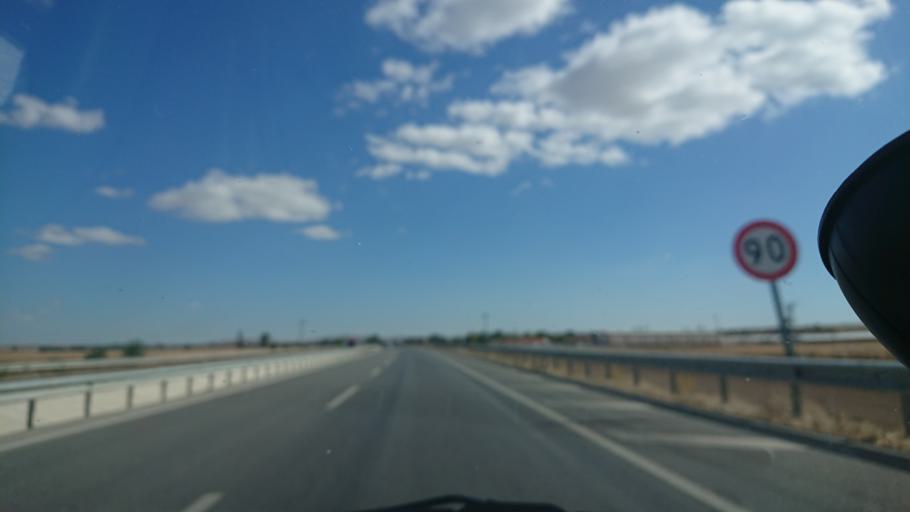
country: TR
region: Eskisehir
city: Mahmudiye
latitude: 39.5448
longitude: 30.9334
